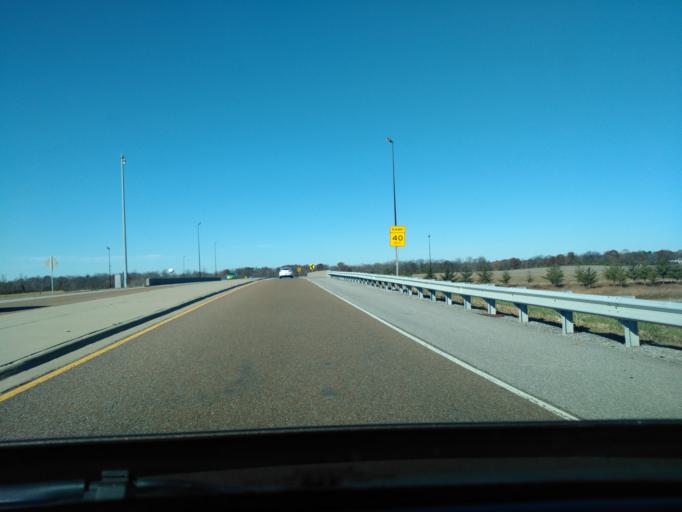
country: US
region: Illinois
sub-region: Madison County
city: Troy
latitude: 38.7183
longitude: -89.9166
